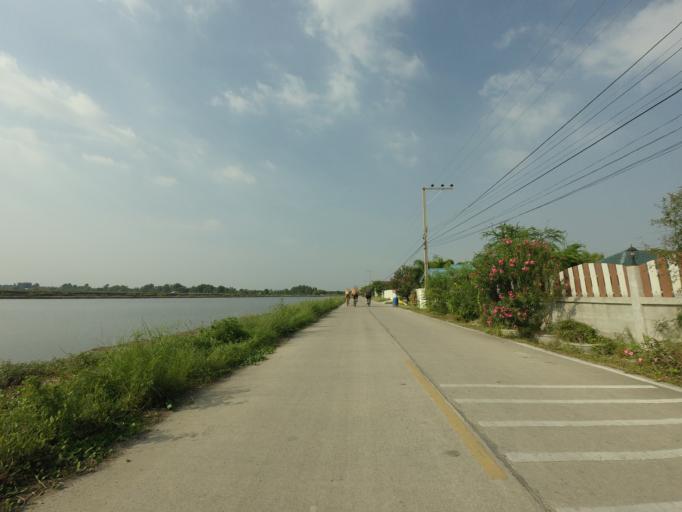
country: TH
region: Samut Sakhon
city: Samut Sakhon
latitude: 13.5044
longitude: 100.3276
